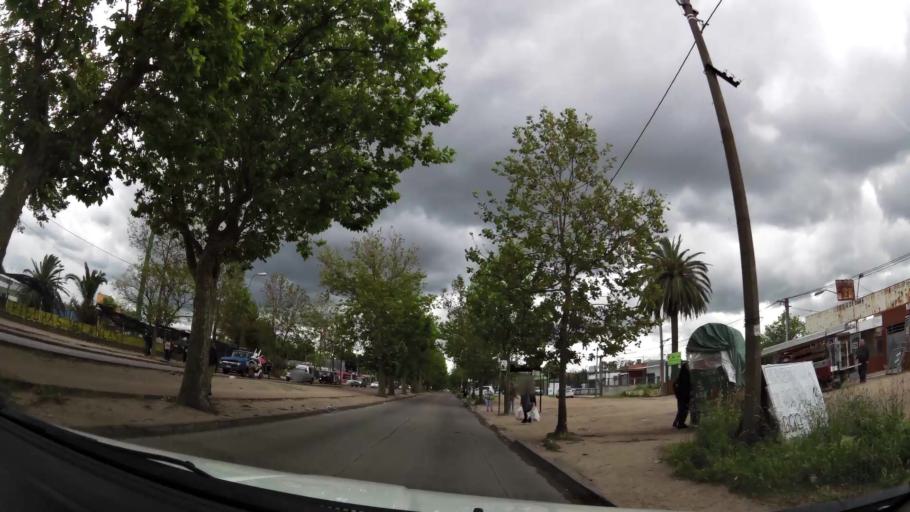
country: UY
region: Canelones
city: Toledo
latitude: -34.8221
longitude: -56.1402
